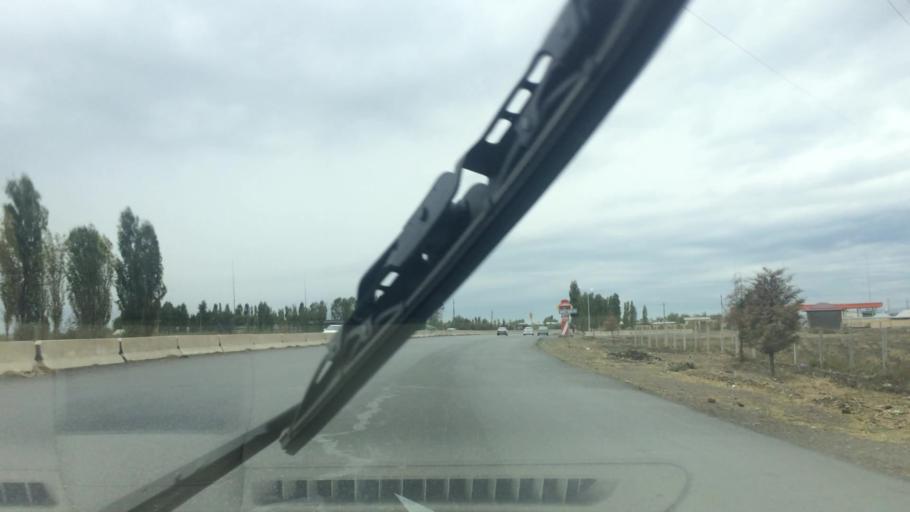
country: UZ
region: Jizzax
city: Jizzax
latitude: 40.0239
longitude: 67.6156
